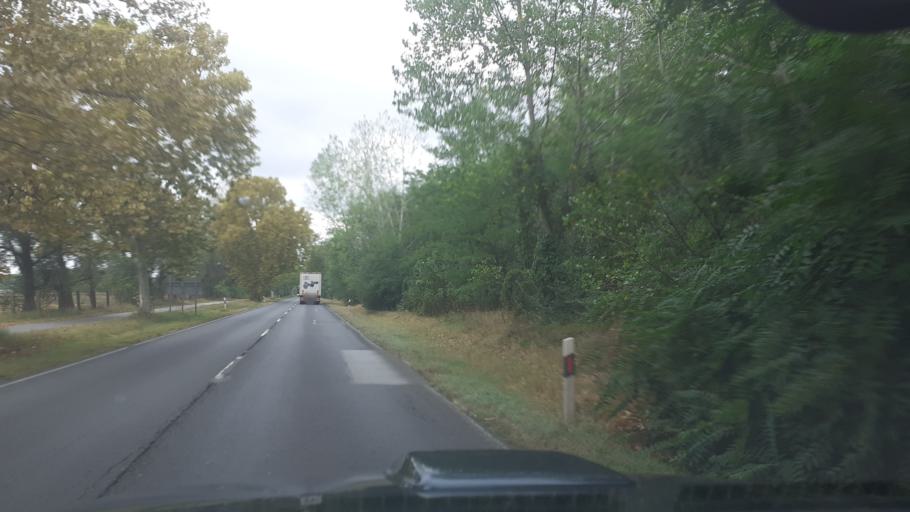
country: HU
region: Bacs-Kiskun
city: Balloszog
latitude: 46.8885
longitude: 19.5890
